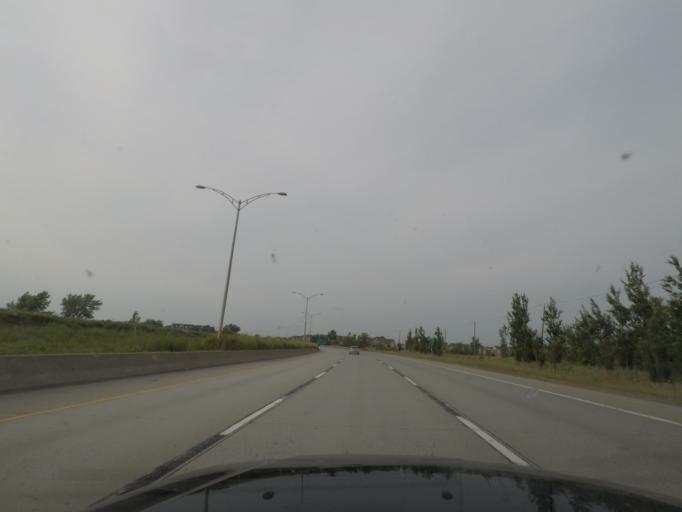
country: CA
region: Quebec
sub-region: Monteregie
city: La Prairie
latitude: 45.4281
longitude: -73.4907
